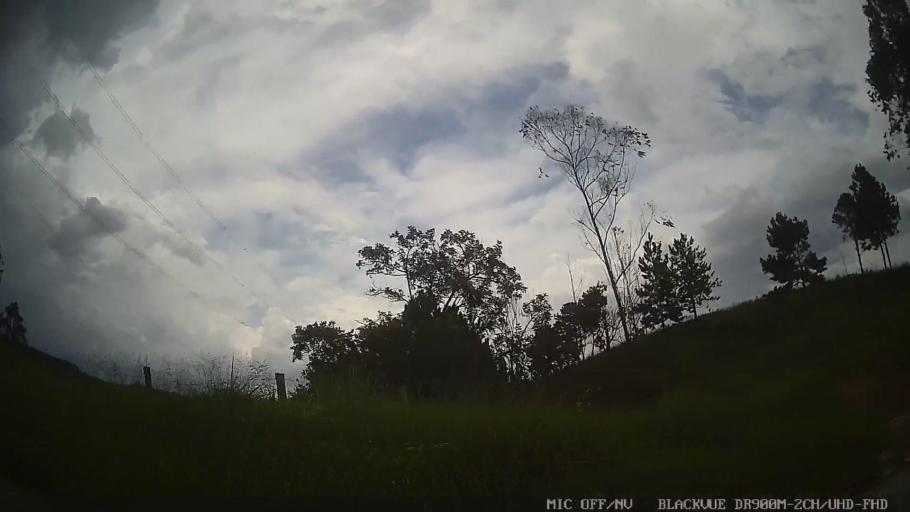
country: BR
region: Sao Paulo
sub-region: Mogi das Cruzes
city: Mogi das Cruzes
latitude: -23.4683
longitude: -46.2285
